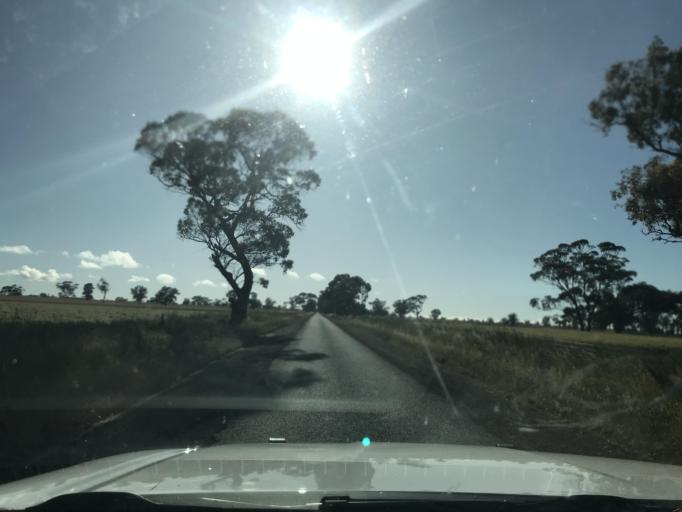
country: AU
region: Victoria
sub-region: Horsham
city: Horsham
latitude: -36.6922
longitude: 141.5465
